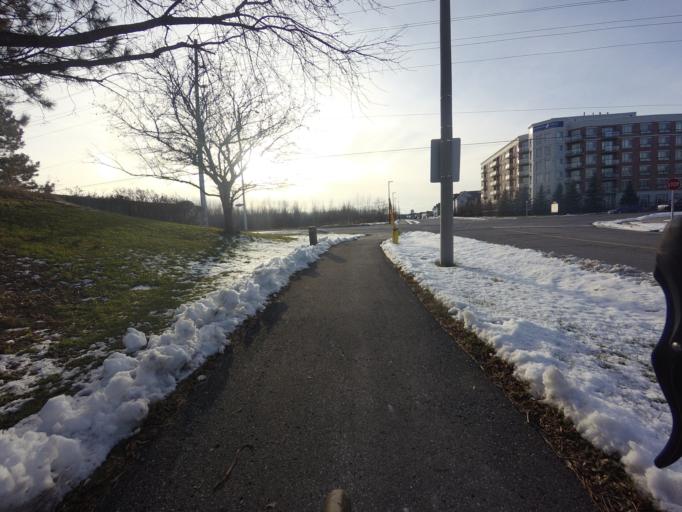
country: CA
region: Ontario
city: Bells Corners
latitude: 45.2741
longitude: -75.8597
